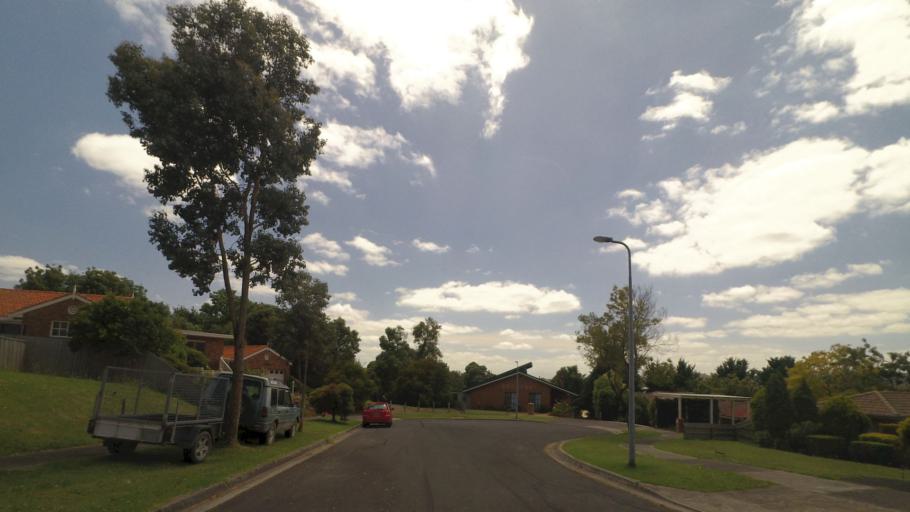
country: AU
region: Victoria
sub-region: Maroondah
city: Bayswater North
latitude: -37.8267
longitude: 145.3011
